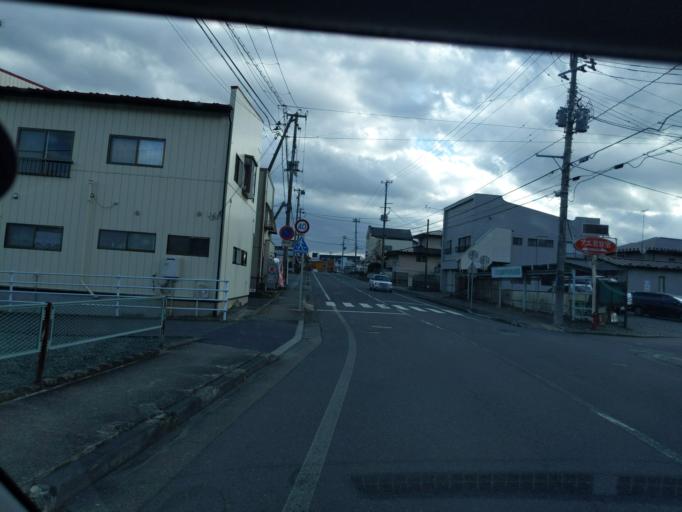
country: JP
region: Iwate
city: Mizusawa
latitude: 39.1302
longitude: 141.1412
